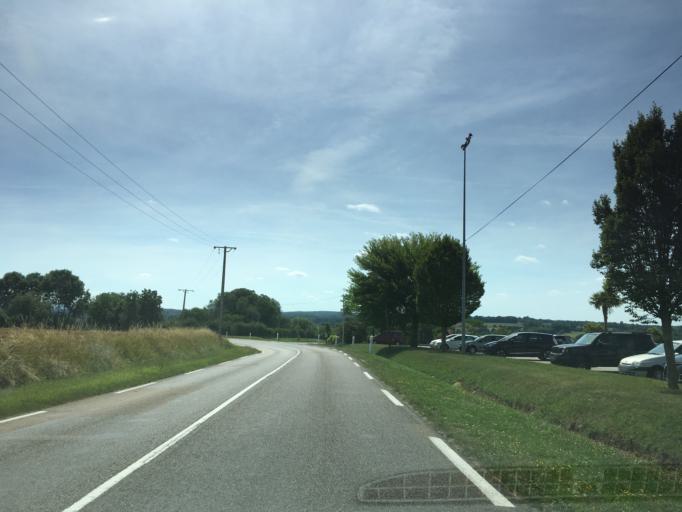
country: FR
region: Bourgogne
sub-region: Departement de l'Yonne
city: Saint-Georges-sur-Baulche
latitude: 47.7942
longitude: 3.5259
